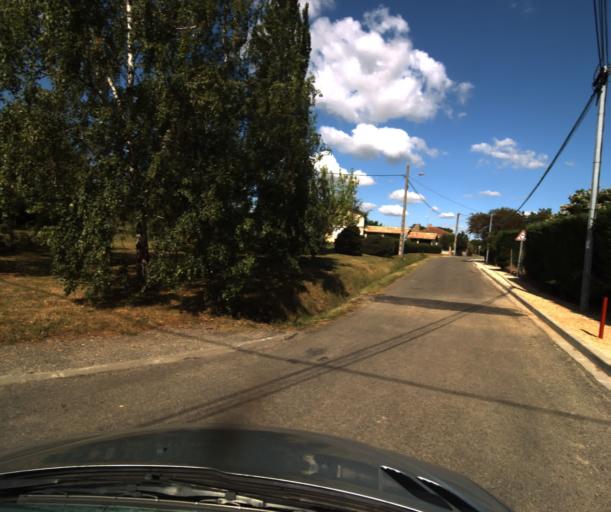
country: FR
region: Midi-Pyrenees
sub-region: Departement du Tarn-et-Garonne
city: Finhan
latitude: 43.9136
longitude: 1.2718
